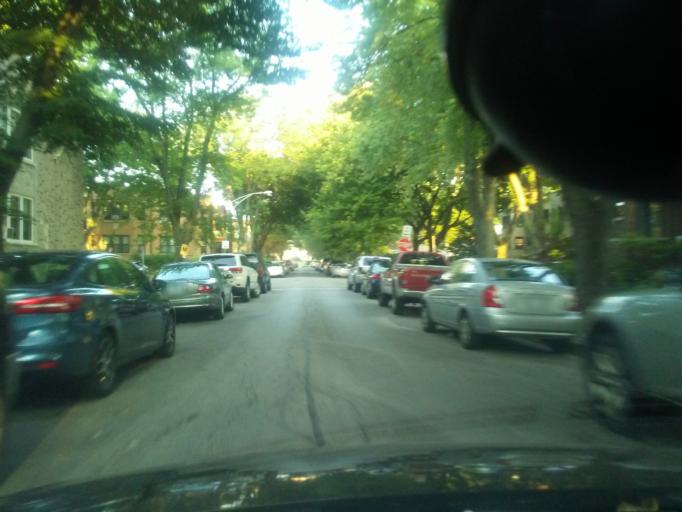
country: US
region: Illinois
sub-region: Cook County
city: Lincolnwood
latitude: 41.9850
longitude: -87.6939
